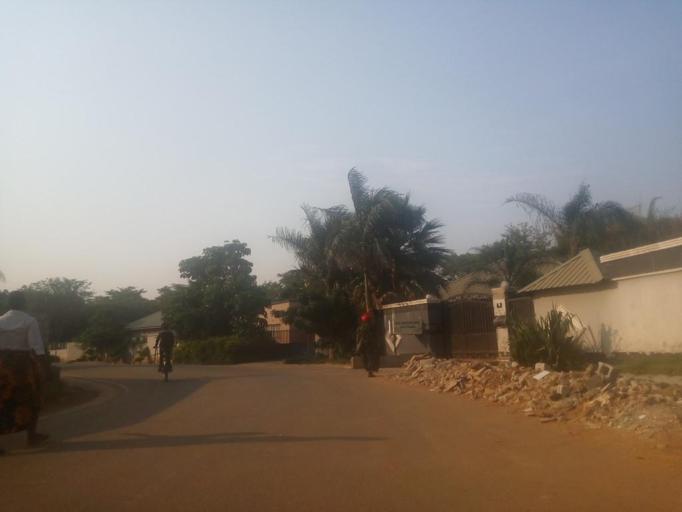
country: ZM
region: Lusaka
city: Lusaka
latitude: -15.3974
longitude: 28.3837
